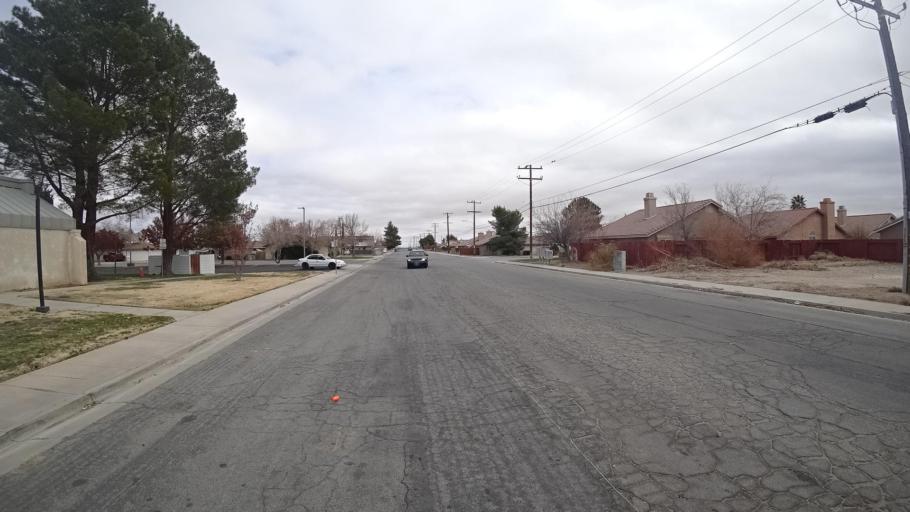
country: US
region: California
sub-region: Kern County
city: Rosamond
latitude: 34.8572
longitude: -118.1668
